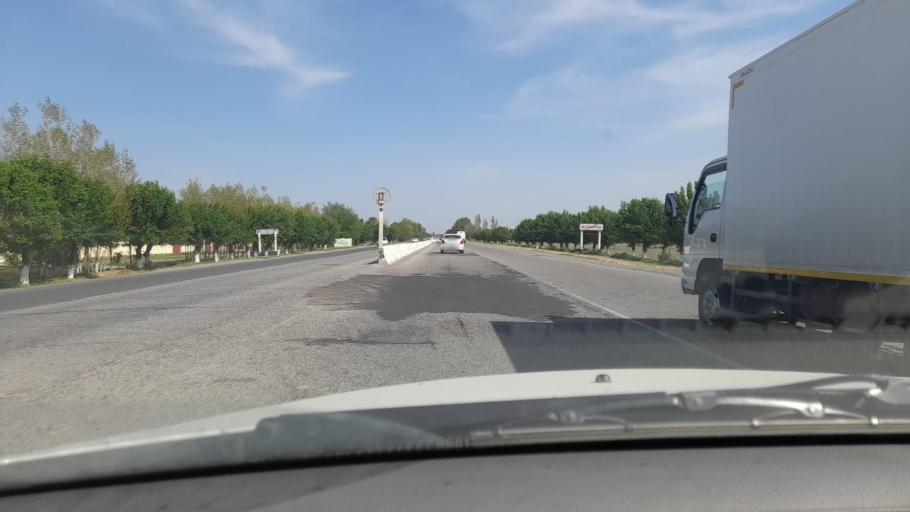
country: UZ
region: Samarqand
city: Chelak
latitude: 39.8487
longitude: 66.8048
